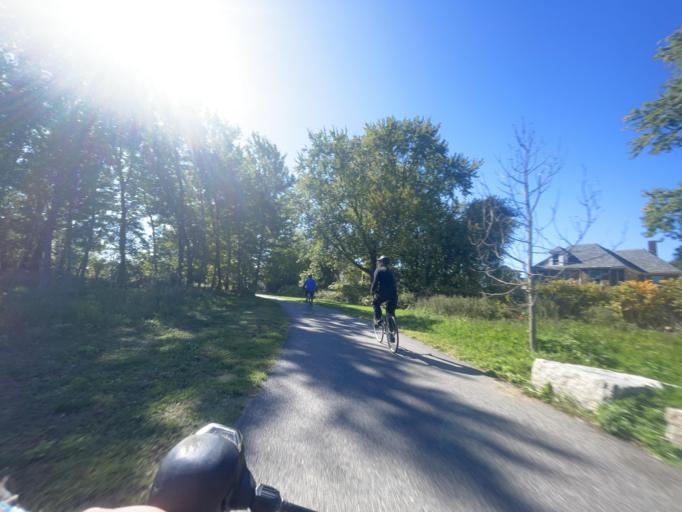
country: US
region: Massachusetts
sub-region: Suffolk County
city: South Boston
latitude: 42.2898
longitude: -71.0391
